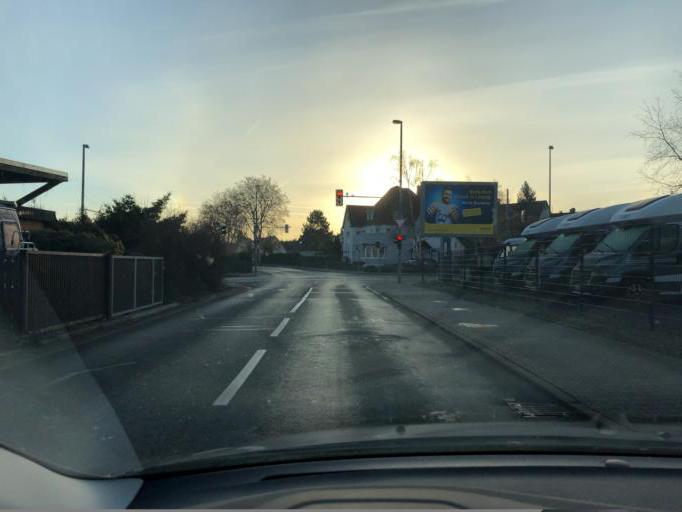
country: DE
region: Saxony
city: Leipzig
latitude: 51.3278
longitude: 12.4370
